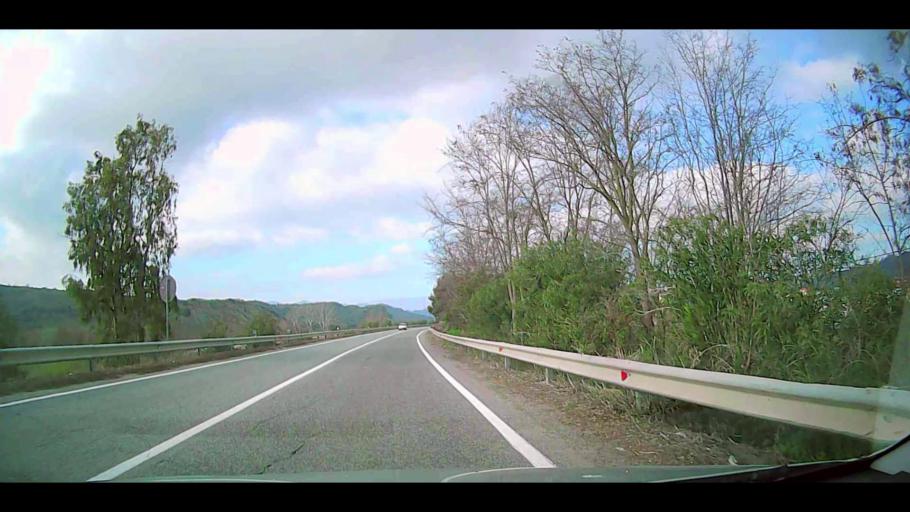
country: IT
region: Calabria
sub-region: Provincia di Crotone
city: Rocca di Neto
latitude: 39.1702
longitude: 16.9879
